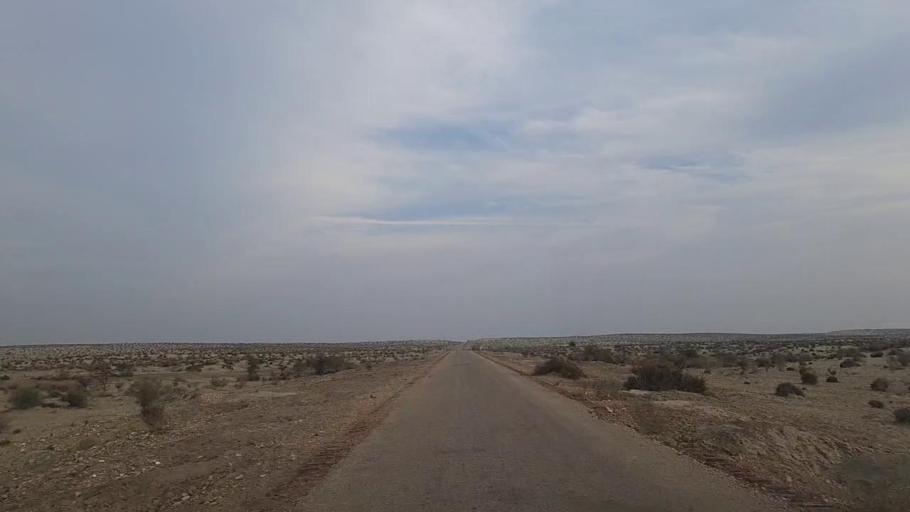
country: PK
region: Sindh
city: Daur
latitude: 26.5130
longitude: 68.5041
